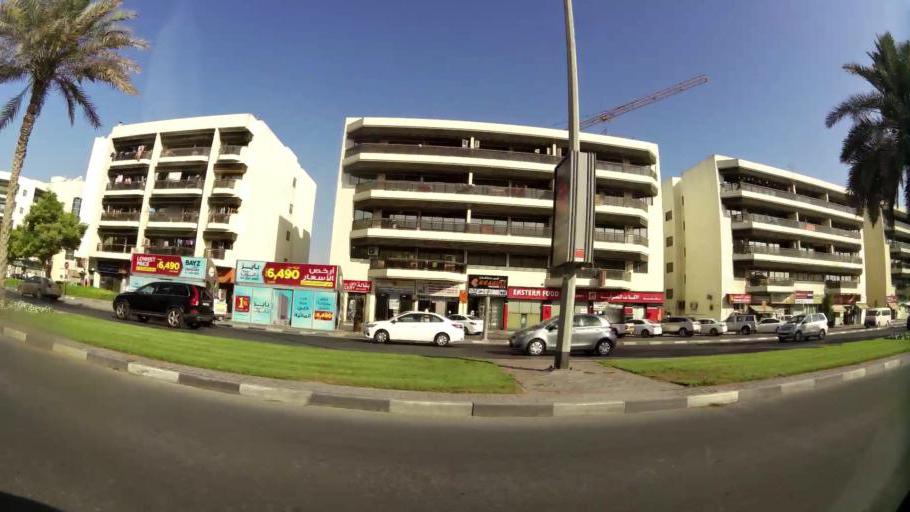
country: AE
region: Ash Shariqah
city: Sharjah
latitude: 25.2827
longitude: 55.3883
